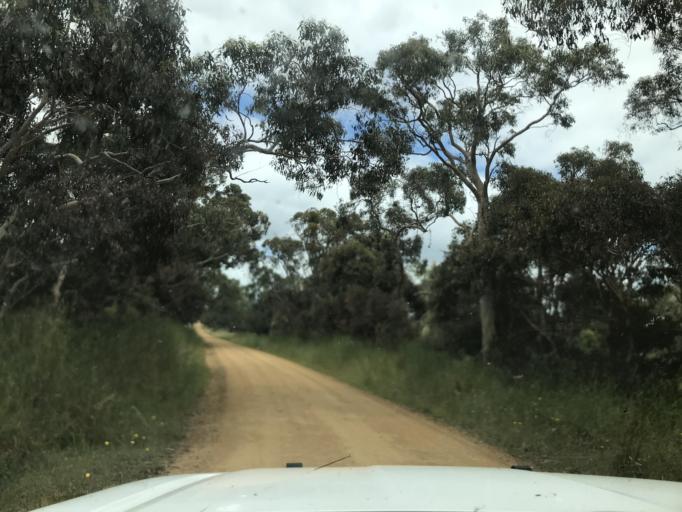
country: AU
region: South Australia
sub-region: Wattle Range
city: Penola
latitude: -37.3006
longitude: 141.0036
